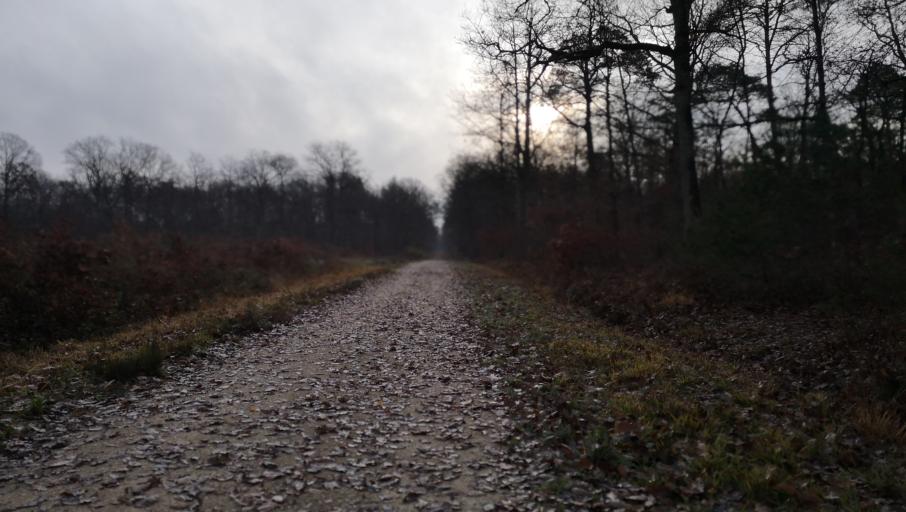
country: FR
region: Centre
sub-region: Departement du Loiret
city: Chanteau
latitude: 47.9465
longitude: 1.9667
